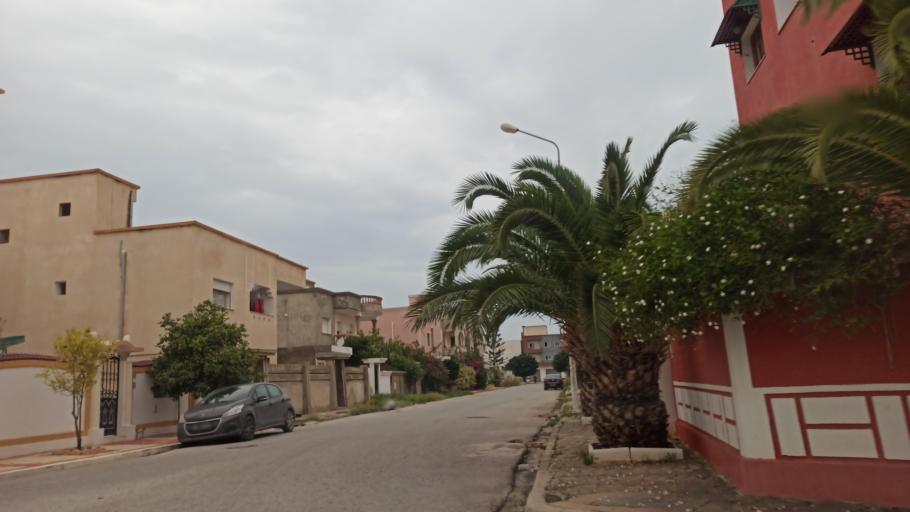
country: TN
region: Tunis
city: Hammam-Lif
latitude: 36.7072
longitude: 10.4144
